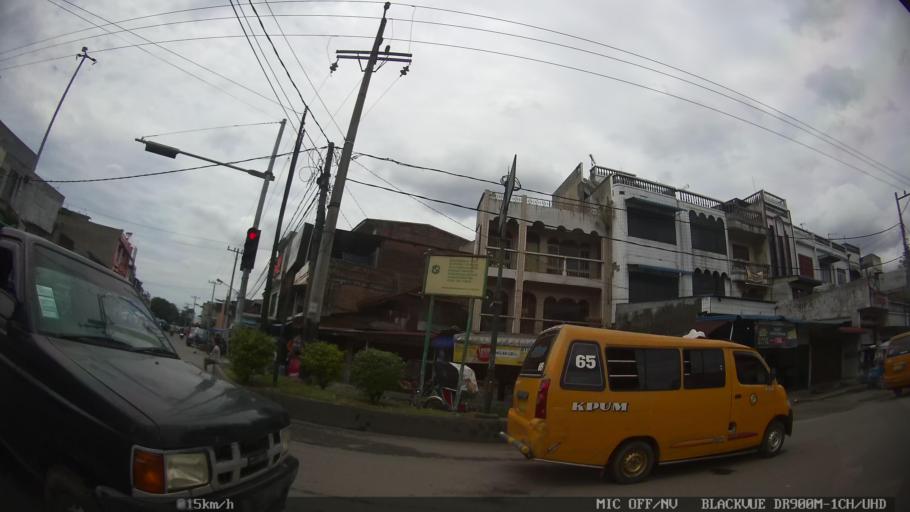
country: ID
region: North Sumatra
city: Sunggal
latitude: 3.5979
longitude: 98.6091
